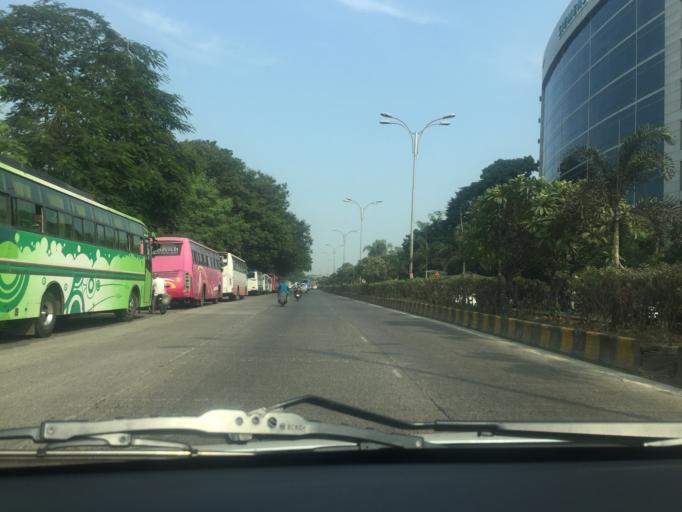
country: IN
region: Maharashtra
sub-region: Thane
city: Airoli
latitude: 19.1529
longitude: 73.0006
